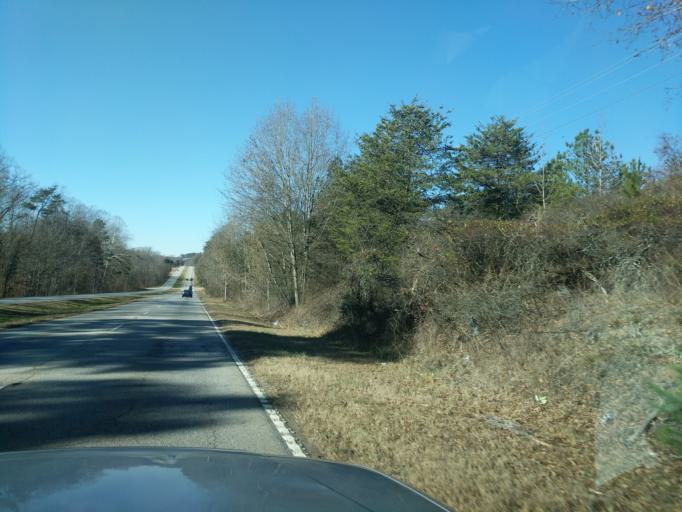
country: US
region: South Carolina
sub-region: Greenville County
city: Parker
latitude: 34.8336
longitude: -82.4644
